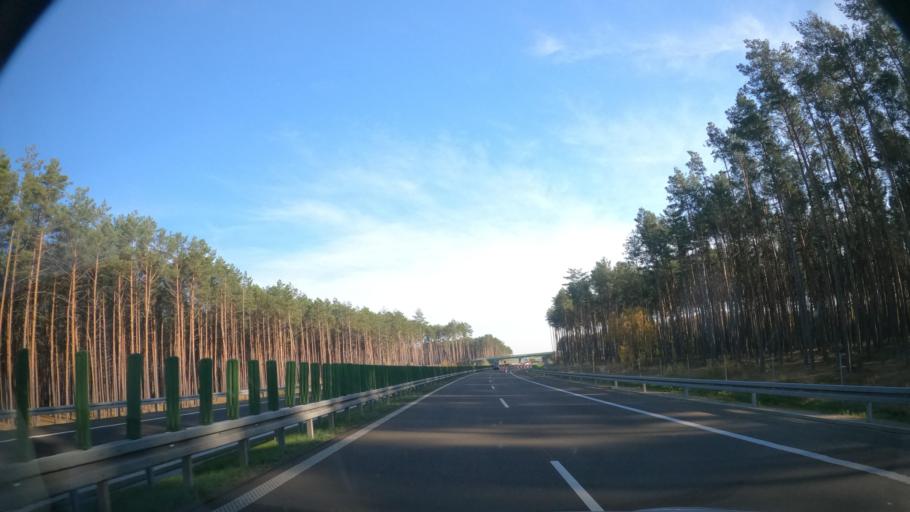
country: PL
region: West Pomeranian Voivodeship
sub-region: Powiat walecki
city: Walcz
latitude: 53.2969
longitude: 16.4364
